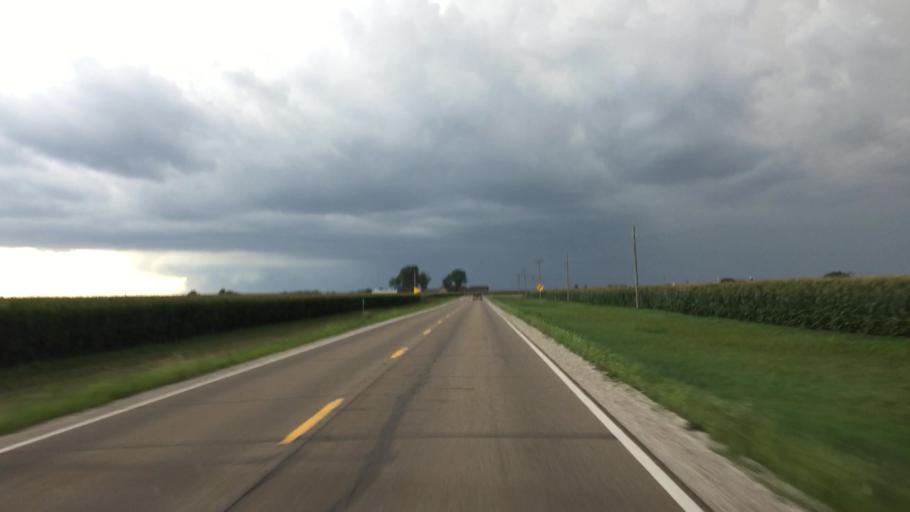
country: US
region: Iowa
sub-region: Henry County
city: New London
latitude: 40.7732
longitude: -91.4694
